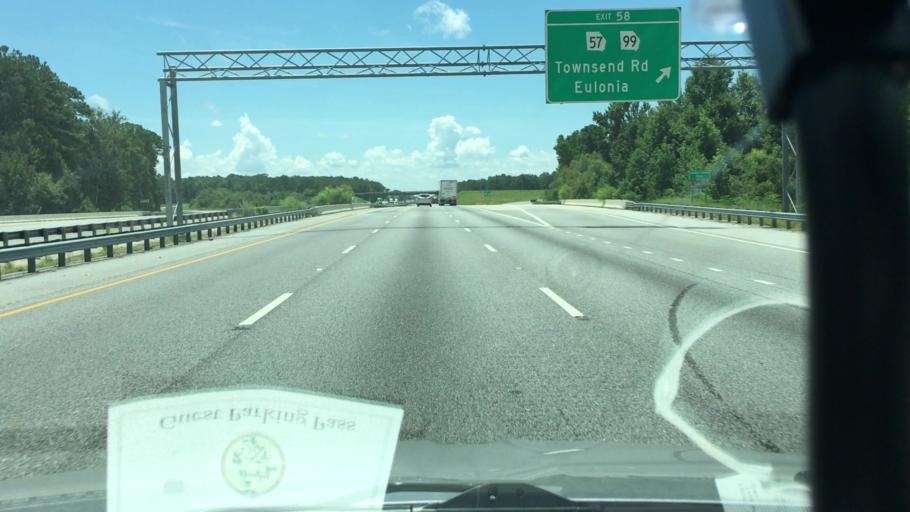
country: US
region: Georgia
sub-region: McIntosh County
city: Darien
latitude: 31.5369
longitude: -81.4450
